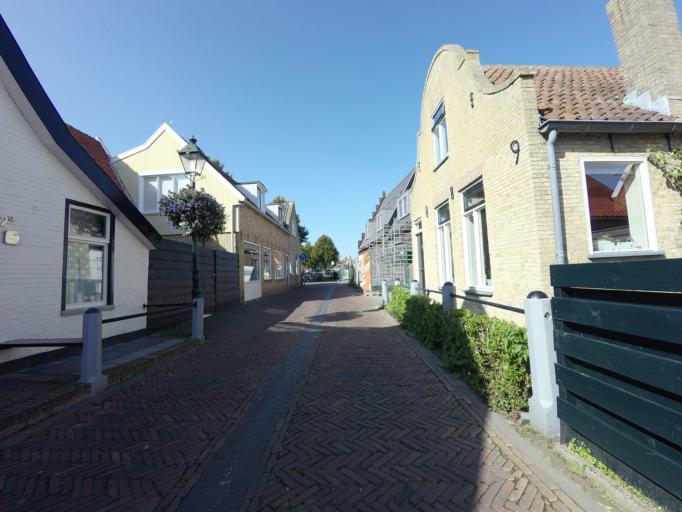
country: NL
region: Friesland
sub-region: Gemeente Terschelling
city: West-Terschelling
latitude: 53.3825
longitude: 5.2856
